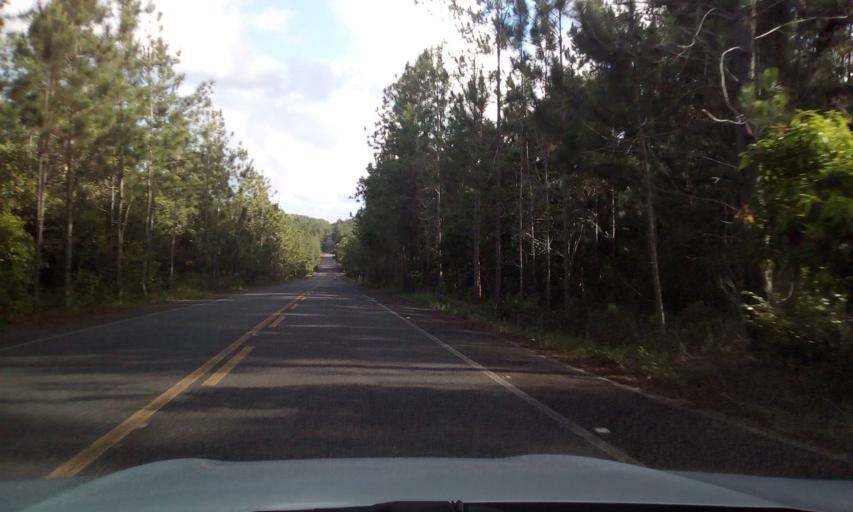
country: BR
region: Bahia
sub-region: Entre Rios
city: Entre Rios
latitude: -12.1124
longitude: -37.7859
